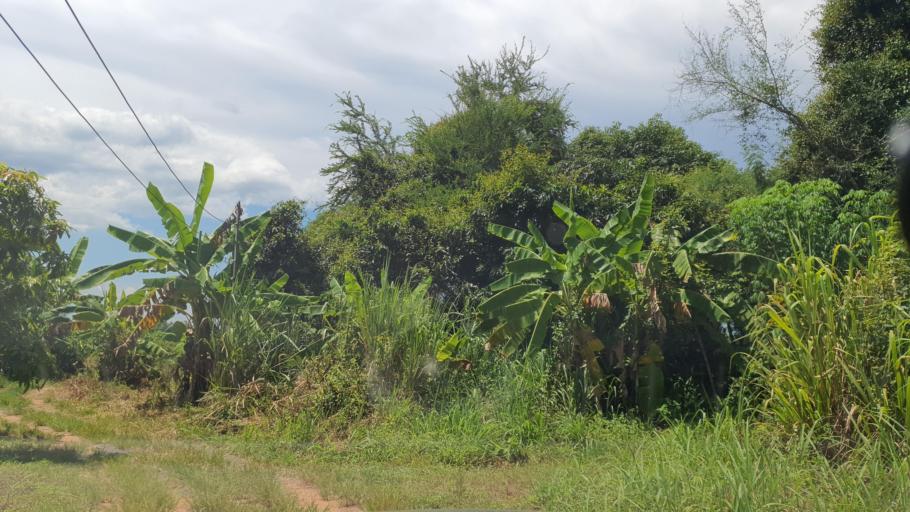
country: TH
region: Chiang Mai
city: Mae On
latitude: 18.7784
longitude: 99.1890
